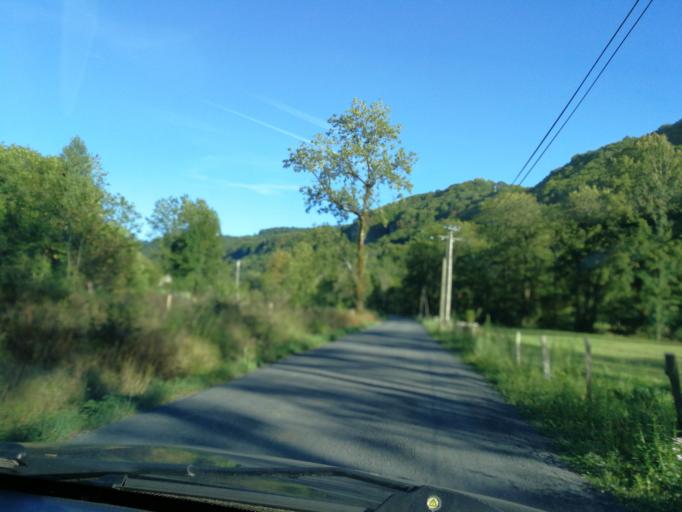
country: FR
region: Auvergne
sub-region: Departement du Cantal
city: Saint-Cernin
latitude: 45.1058
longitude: 2.5226
